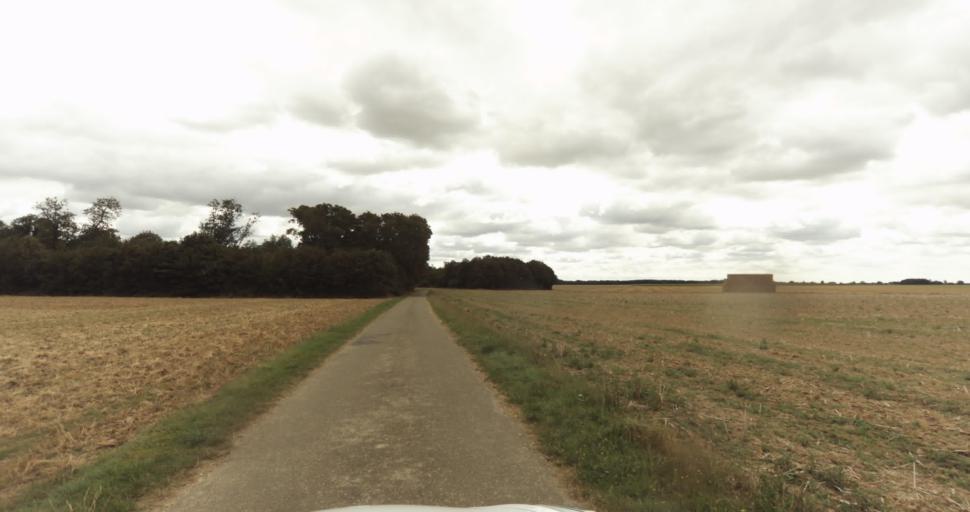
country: FR
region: Haute-Normandie
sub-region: Departement de l'Eure
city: Nonancourt
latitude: 48.8159
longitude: 1.1568
